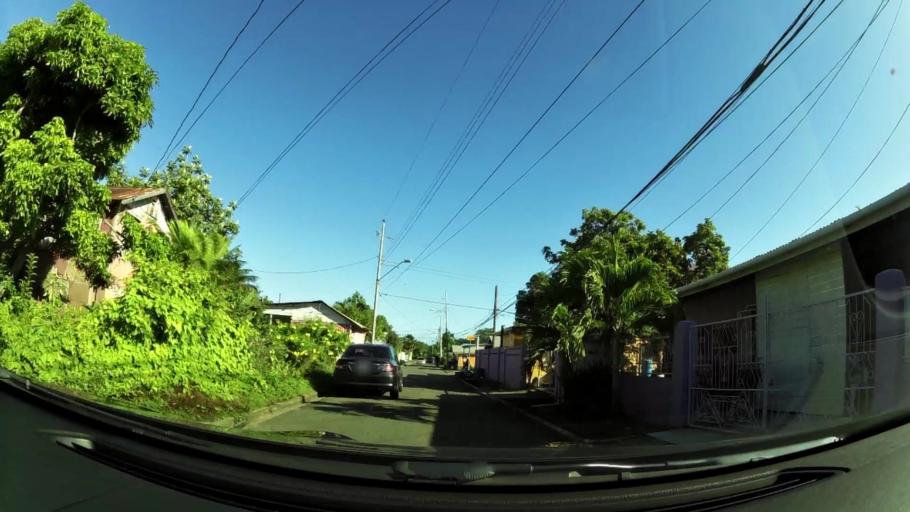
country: TT
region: Tobago
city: Scarborough
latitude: 11.1552
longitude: -60.8235
